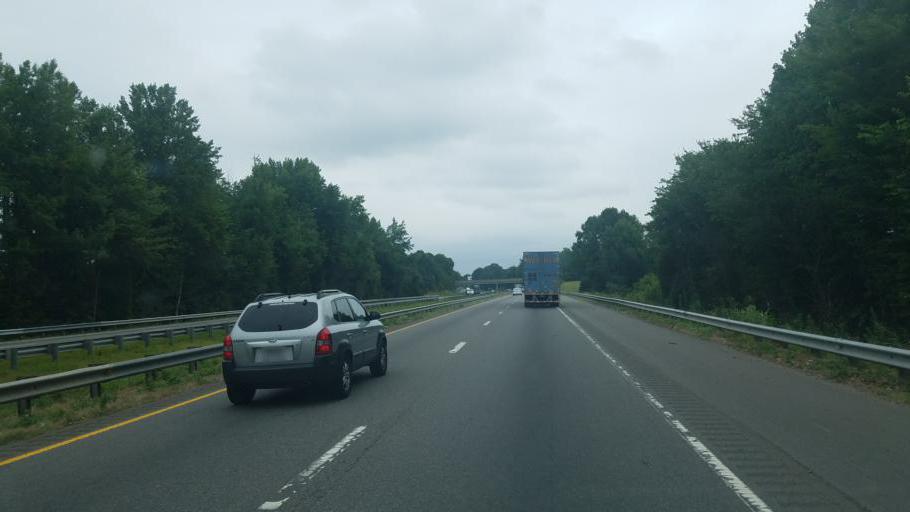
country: US
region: North Carolina
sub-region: Iredell County
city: Troutman
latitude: 35.6770
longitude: -80.8549
